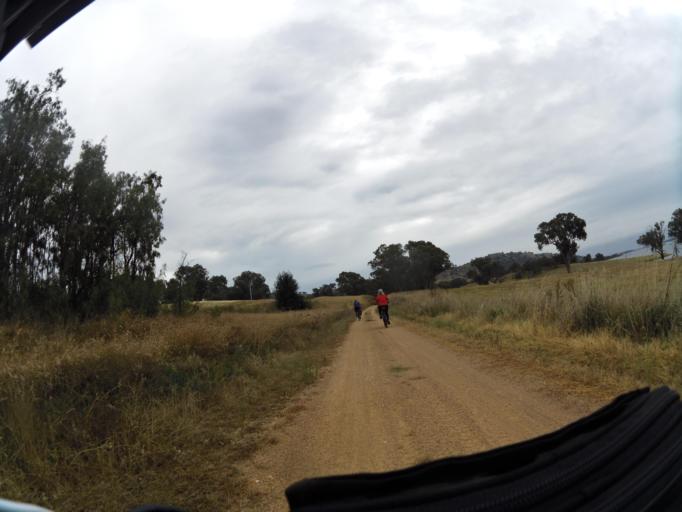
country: AU
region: New South Wales
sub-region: Albury Municipality
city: East Albury
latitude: -36.2013
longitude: 147.0461
